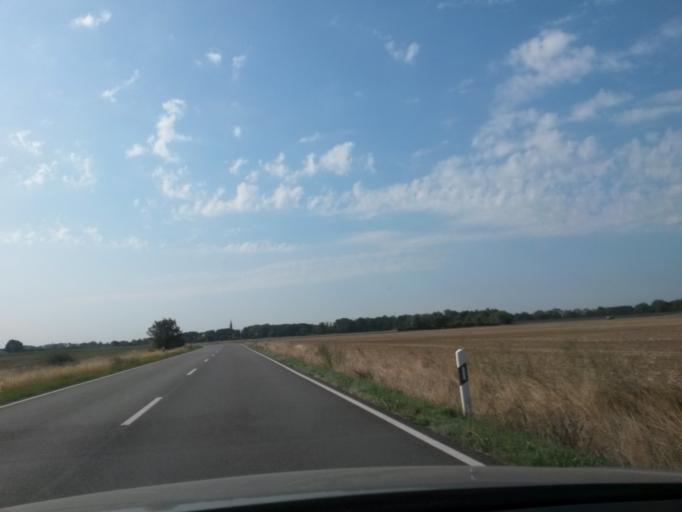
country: DE
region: Saxony-Anhalt
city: Jerichow
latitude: 52.5173
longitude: 12.0158
